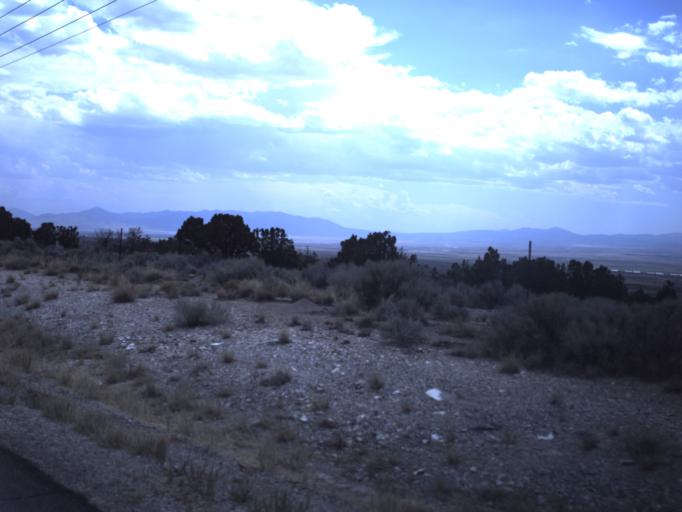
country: US
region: Utah
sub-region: Tooele County
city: Tooele
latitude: 40.3313
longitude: -112.2950
